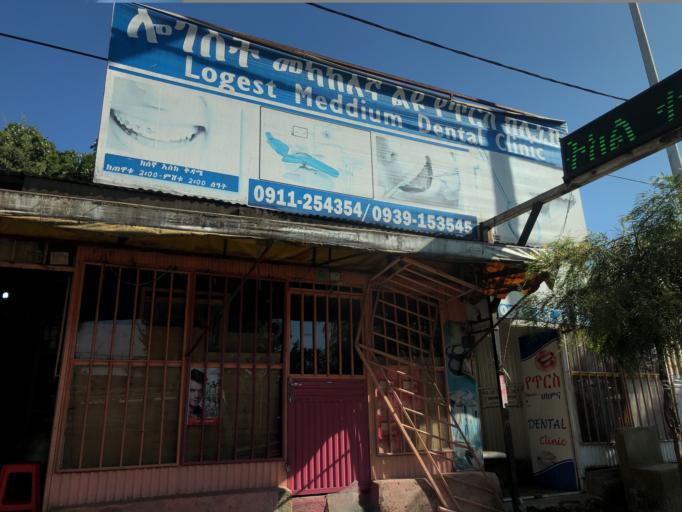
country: ET
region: Adis Abeba
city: Addis Ababa
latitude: 9.0276
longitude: 38.7739
